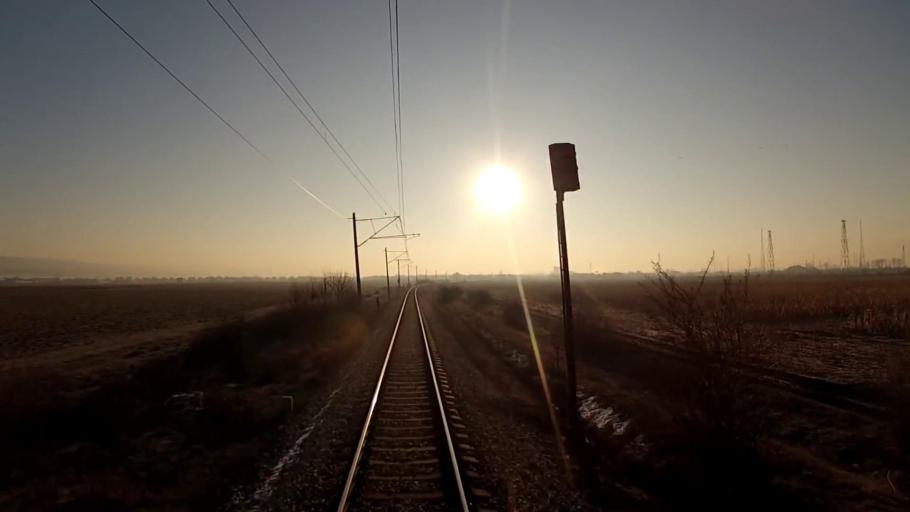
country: BG
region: Sofiya
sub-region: Obshtina Kostinbrod
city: Kostinbrod
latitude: 42.8098
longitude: 23.1953
